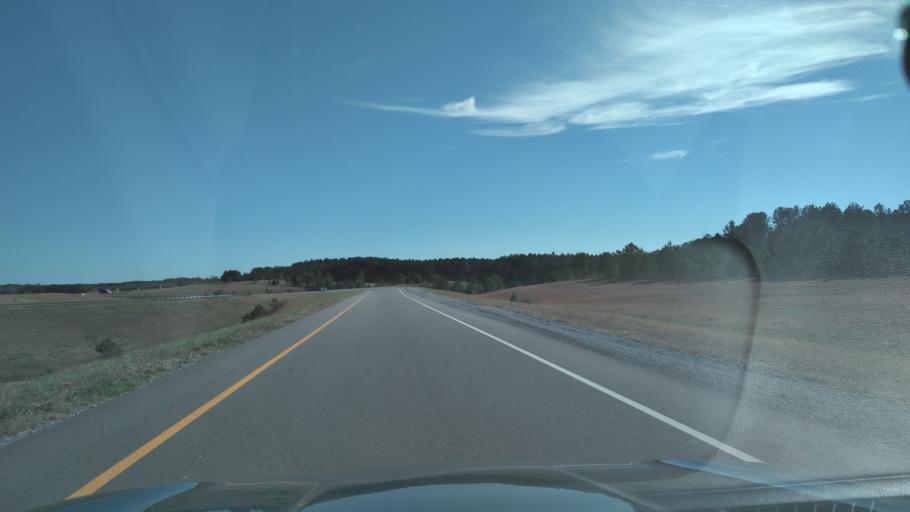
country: US
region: Alabama
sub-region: Walker County
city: Jasper
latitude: 33.8557
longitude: -87.3523
